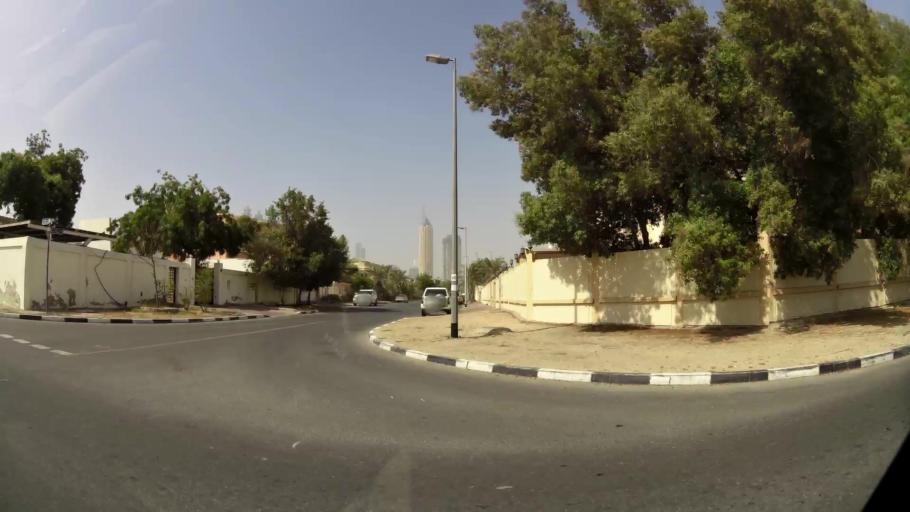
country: AE
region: Dubai
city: Dubai
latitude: 25.1711
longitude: 55.2545
